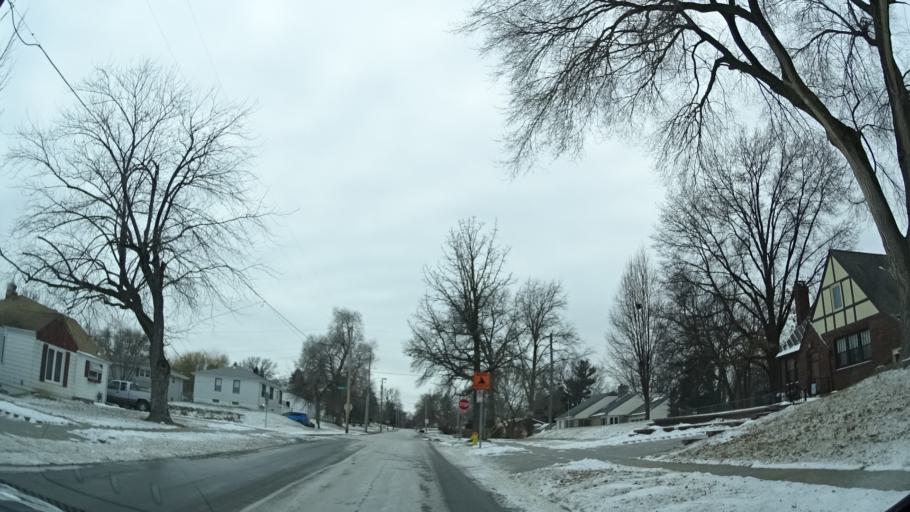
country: US
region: Nebraska
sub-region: Douglas County
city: Omaha
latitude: 41.2347
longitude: -95.9855
